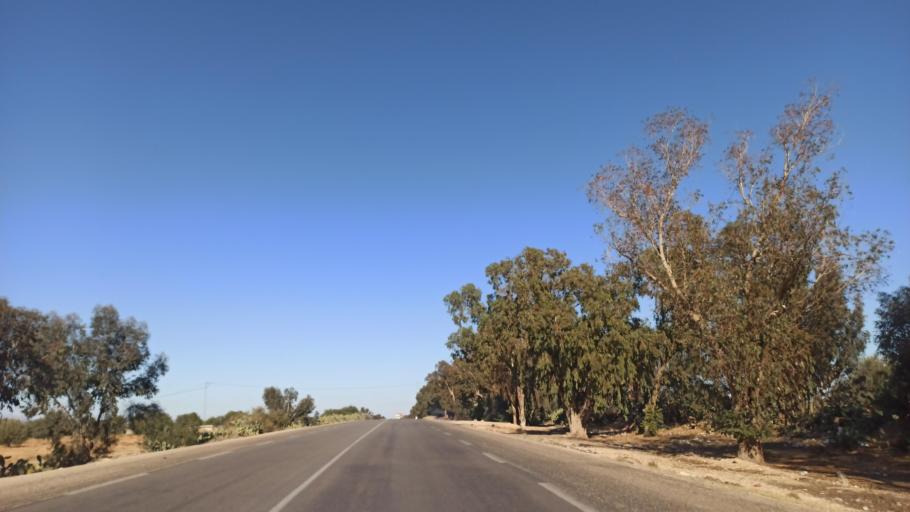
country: TN
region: Sidi Bu Zayd
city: Jilma
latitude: 35.1642
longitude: 9.3683
